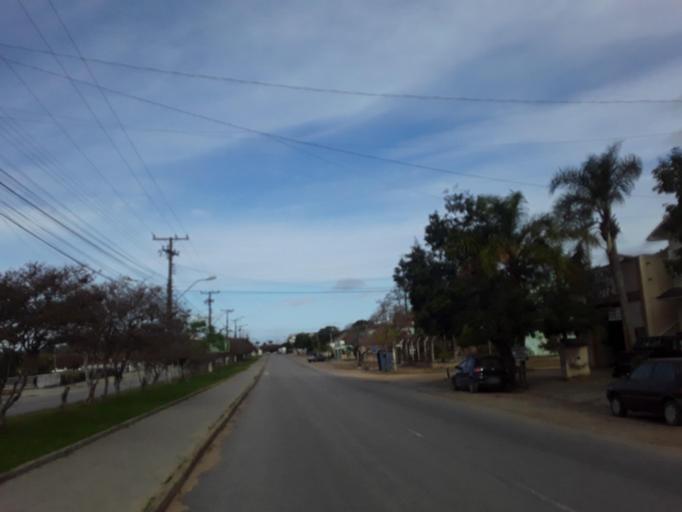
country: BR
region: Rio Grande do Sul
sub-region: Sao Lourenco Do Sul
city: Sao Lourenco do Sul
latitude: -31.3496
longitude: -51.9916
